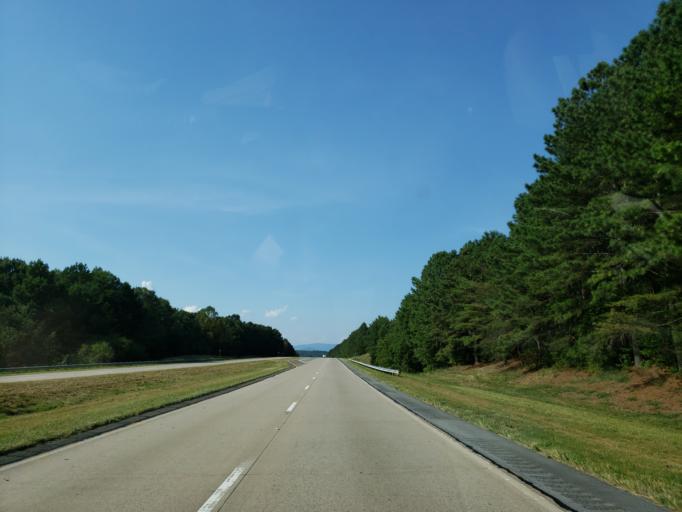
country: US
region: Georgia
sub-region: Gilmer County
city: Ellijay
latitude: 34.6060
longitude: -84.5182
